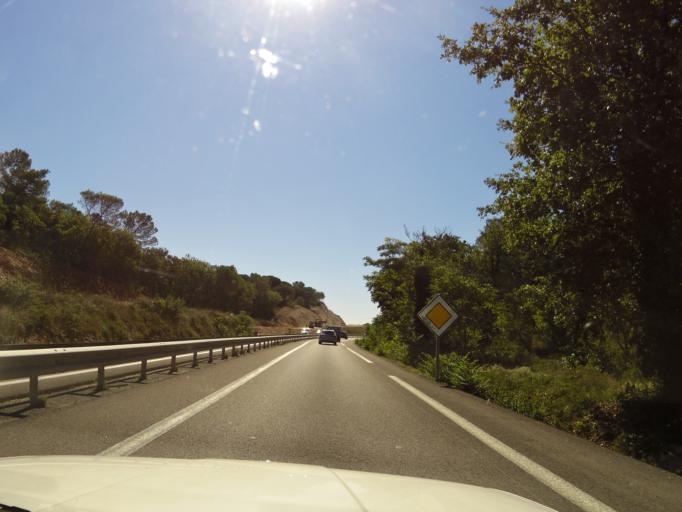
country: FR
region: Languedoc-Roussillon
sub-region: Departement du Gard
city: La Calmette
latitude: 43.9119
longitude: 4.2679
